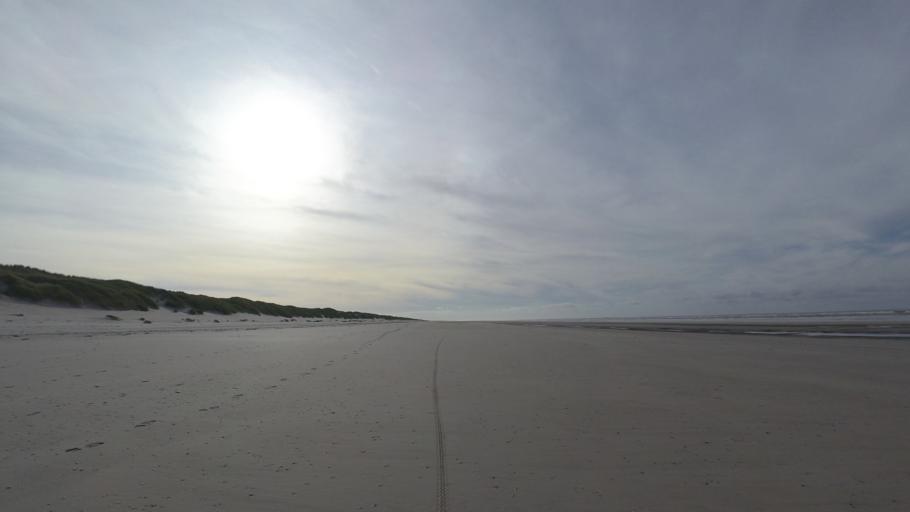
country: NL
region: Friesland
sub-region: Gemeente Dongeradeel
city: Holwerd
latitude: 53.4664
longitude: 5.8834
